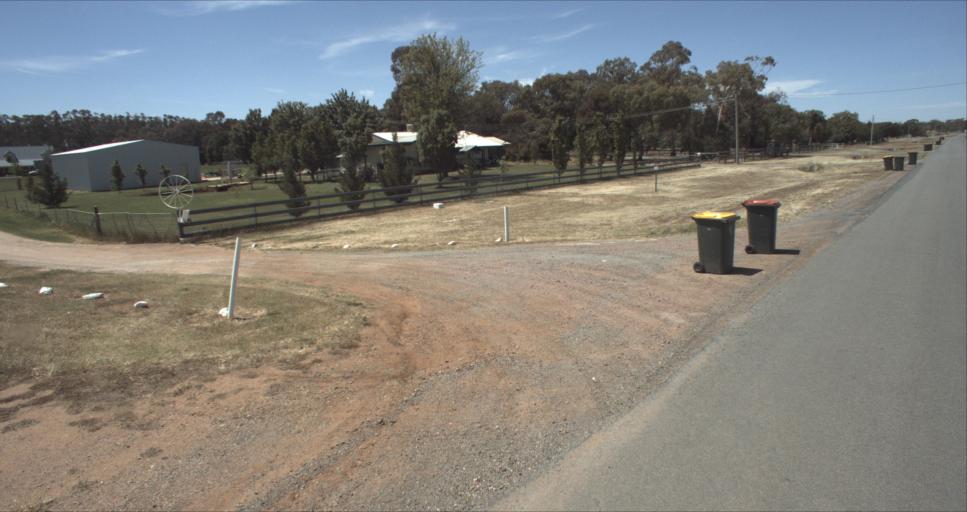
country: AU
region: New South Wales
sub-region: Leeton
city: Leeton
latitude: -34.5853
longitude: 146.4153
